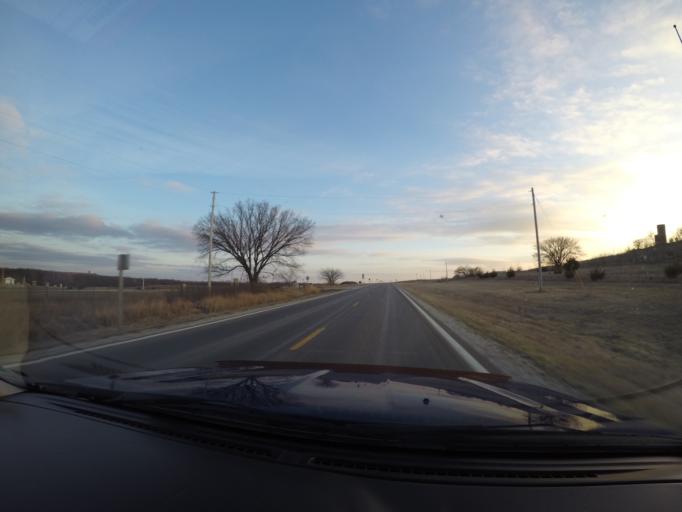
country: US
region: Kansas
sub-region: Chase County
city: Cottonwood Falls
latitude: 38.4053
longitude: -96.5565
